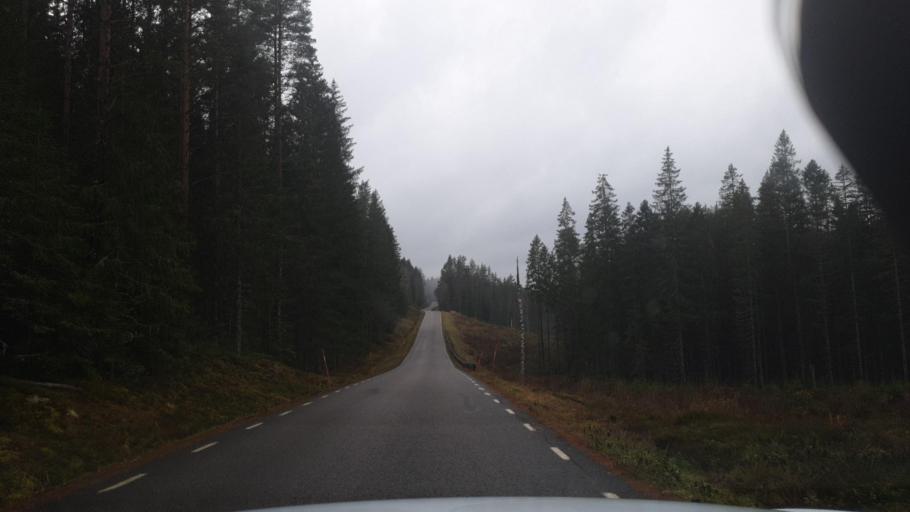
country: SE
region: Vaermland
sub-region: Arvika Kommun
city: Arvika
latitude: 59.5736
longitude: 12.4753
